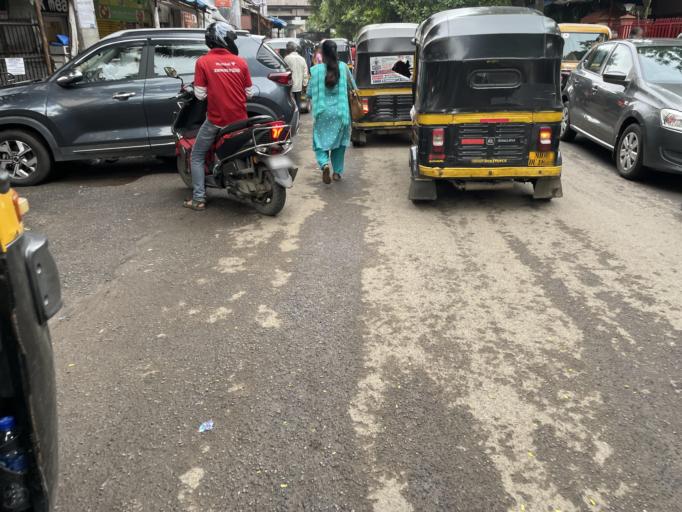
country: IN
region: Maharashtra
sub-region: Mumbai Suburban
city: Borivli
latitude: 19.2301
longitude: 72.8640
